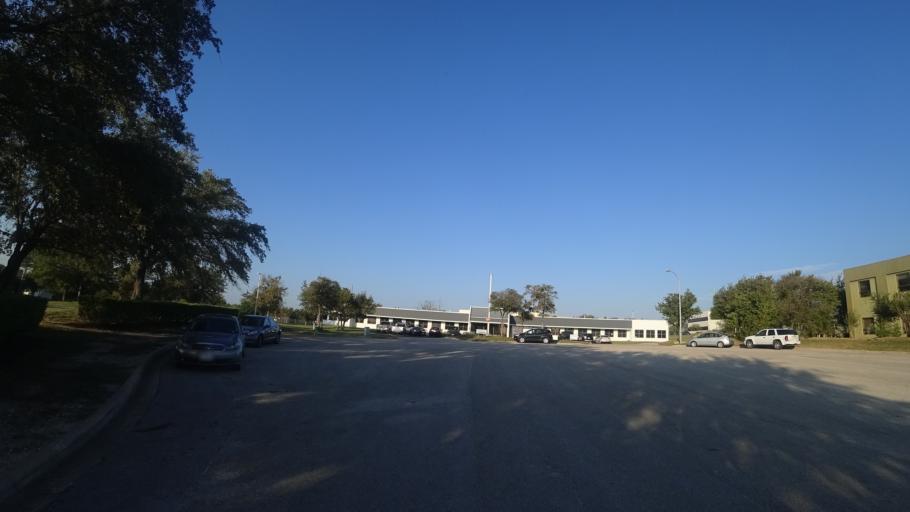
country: US
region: Texas
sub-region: Travis County
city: Austin
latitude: 30.3339
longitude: -97.6829
